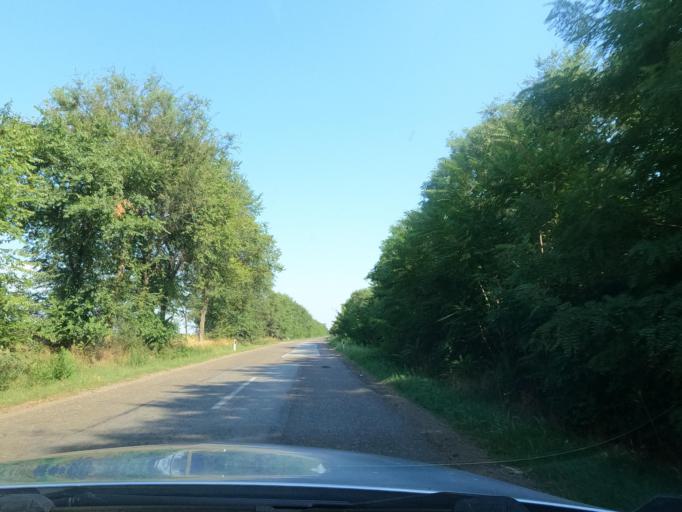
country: RS
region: Autonomna Pokrajina Vojvodina
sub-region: Juznobacki Okrug
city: Becej
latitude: 45.6639
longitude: 19.9439
